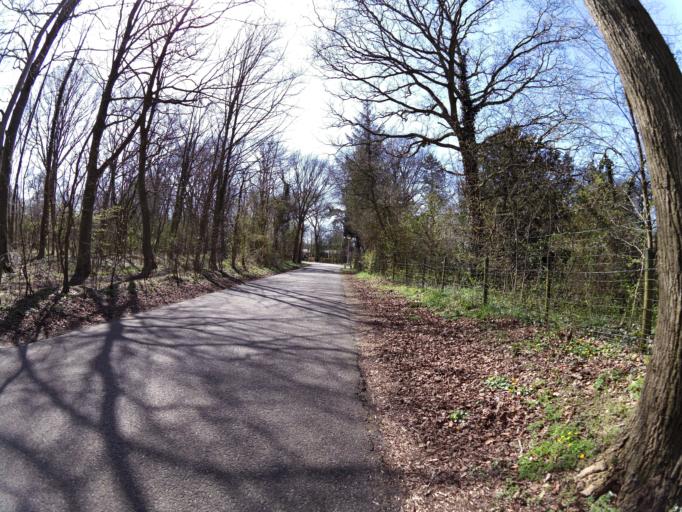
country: NL
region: South Holland
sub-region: Gemeente Hellevoetsluis
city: Nieuw-Helvoet
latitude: 51.9032
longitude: 4.0722
